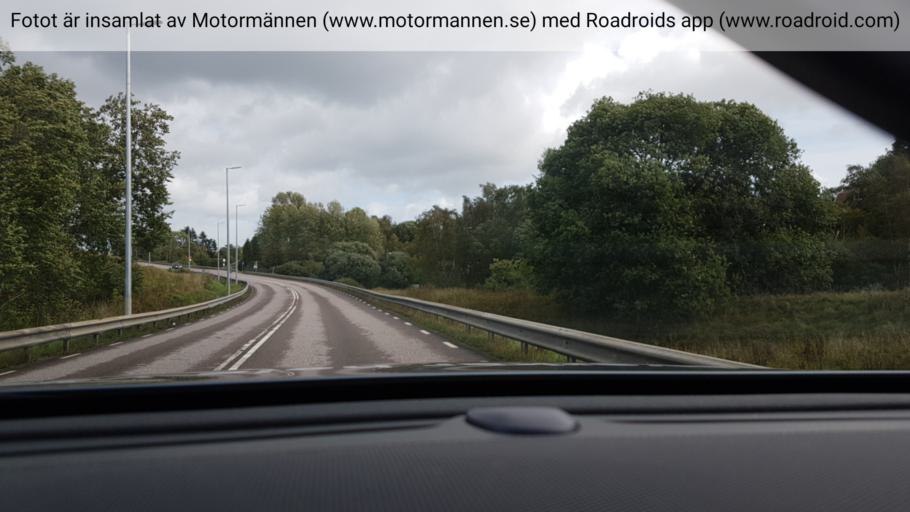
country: SE
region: Vaestra Goetaland
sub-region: Partille Kommun
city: Partille
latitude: 57.8001
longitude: 12.1514
